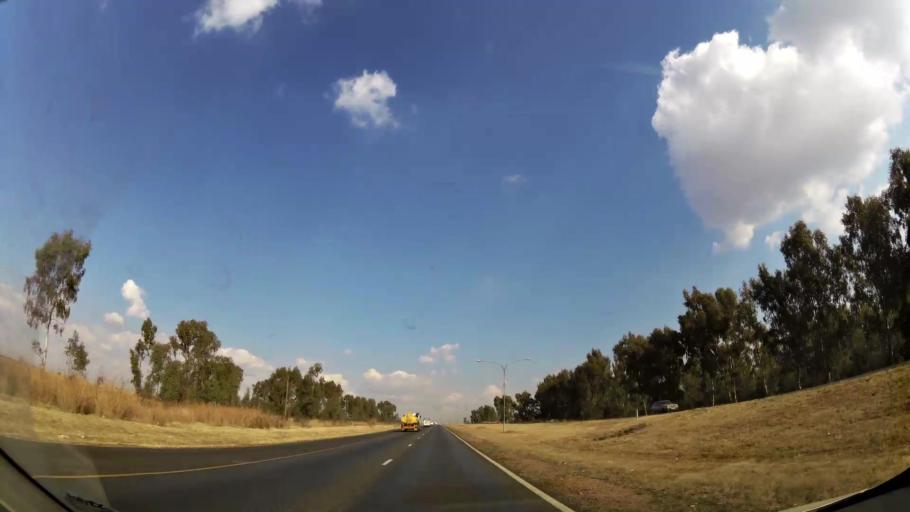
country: ZA
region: Gauteng
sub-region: Ekurhuleni Metropolitan Municipality
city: Brakpan
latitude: -26.3336
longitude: 28.3402
